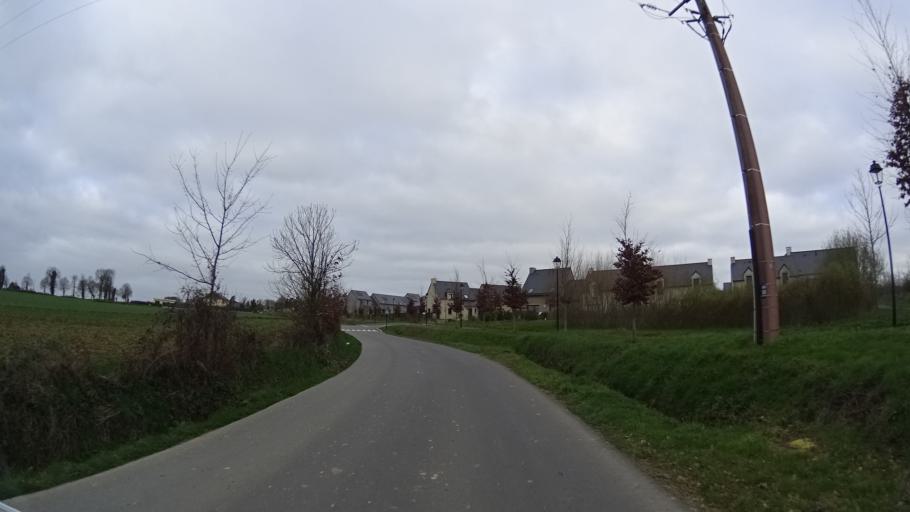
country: FR
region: Brittany
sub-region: Departement d'Ille-et-Vilaine
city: Saint-Gilles
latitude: 48.1766
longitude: -1.8572
